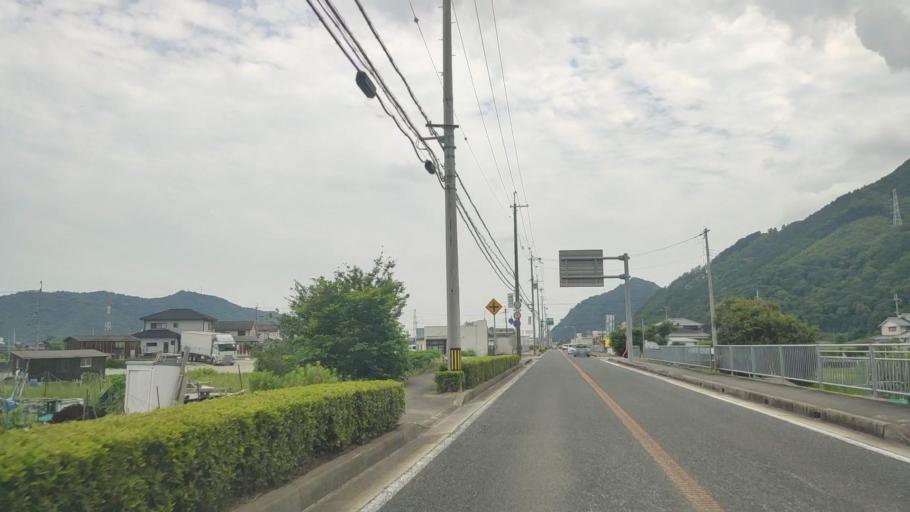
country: JP
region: Hyogo
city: Tatsunocho-tominaga
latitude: 34.8915
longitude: 134.5464
